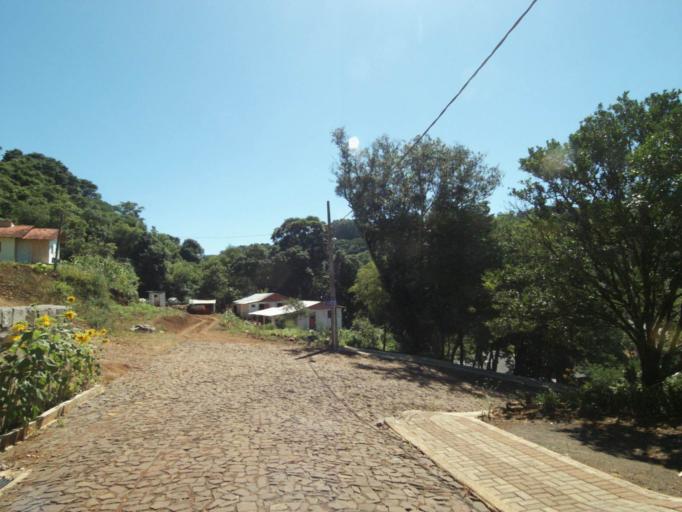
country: BR
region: Parana
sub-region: Ampere
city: Ampere
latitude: -26.1782
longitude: -53.3625
